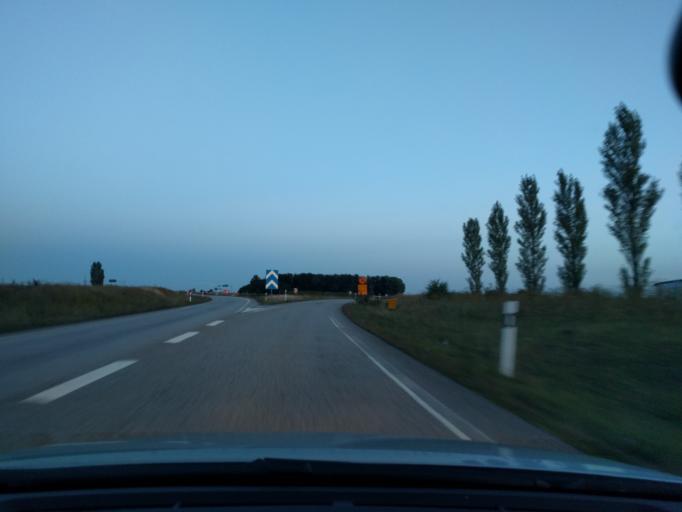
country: SE
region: Skane
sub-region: Malmo
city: Tygelsjo
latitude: 55.5506
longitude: 13.0001
